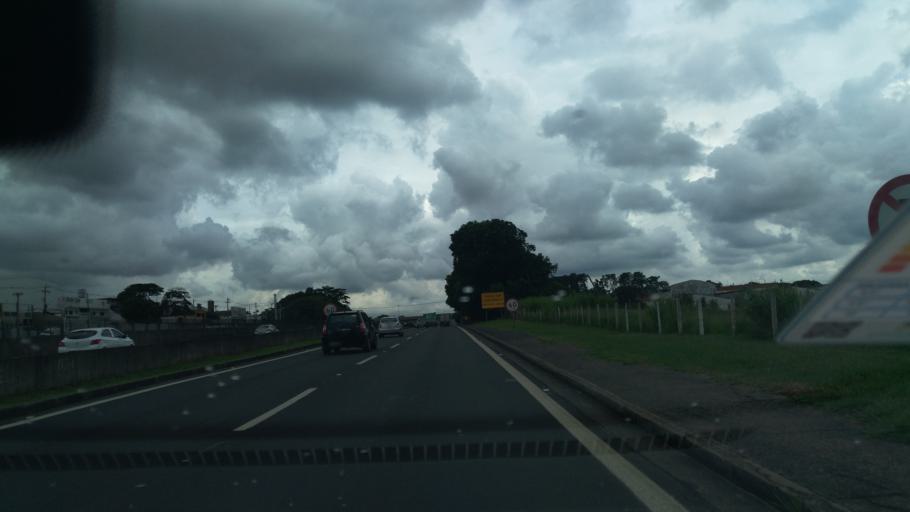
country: BR
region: Sao Paulo
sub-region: Campinas
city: Campinas
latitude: -22.8891
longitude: -47.1131
